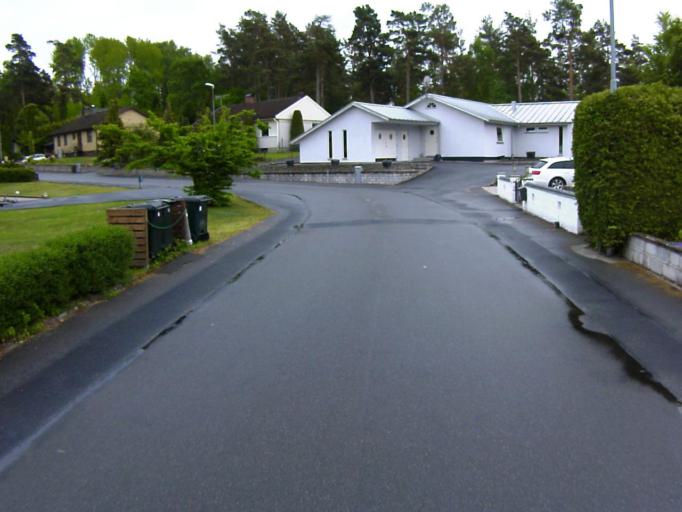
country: SE
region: Skane
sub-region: Kristianstads Kommun
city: Degeberga
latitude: 55.8308
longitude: 14.0921
